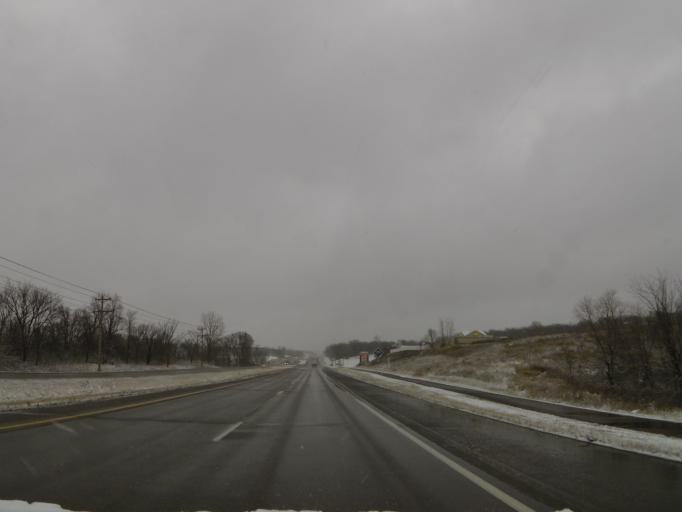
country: US
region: Minnesota
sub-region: Scott County
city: Prior Lake
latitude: 44.7467
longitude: -93.4338
